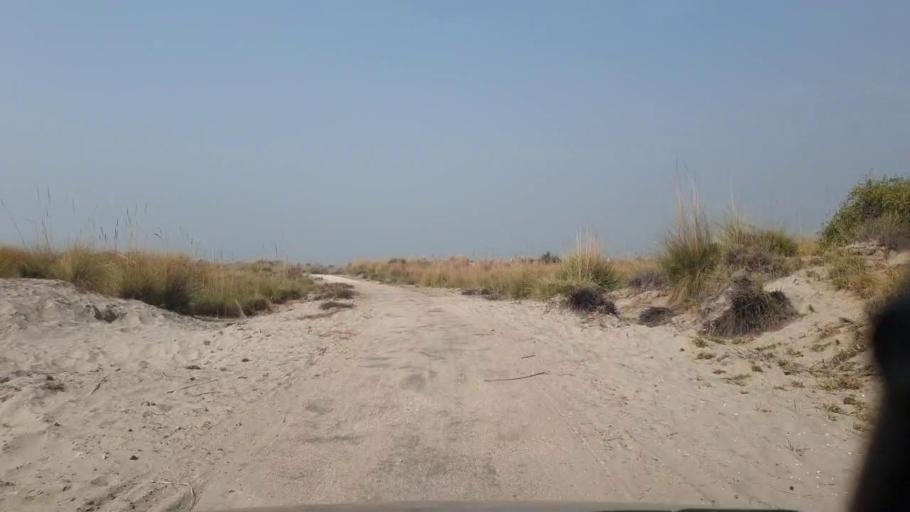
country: PK
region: Sindh
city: Shahdadpur
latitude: 26.0344
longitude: 68.5235
